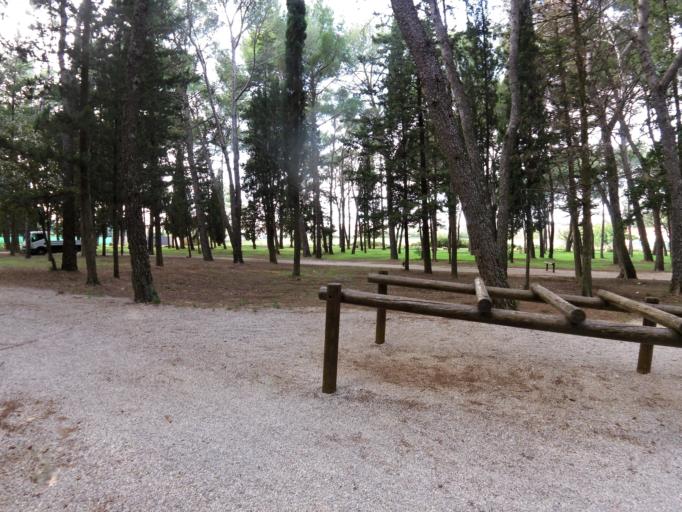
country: FR
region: Languedoc-Roussillon
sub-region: Departement de l'Herault
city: Lunel
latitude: 43.6915
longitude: 4.1283
